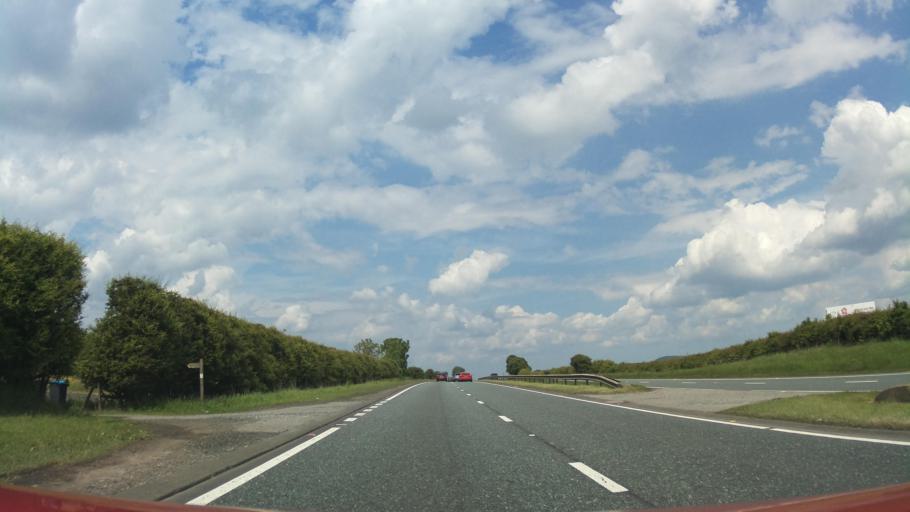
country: GB
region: England
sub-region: North Yorkshire
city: Thirsk
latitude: 54.3231
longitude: -1.3387
